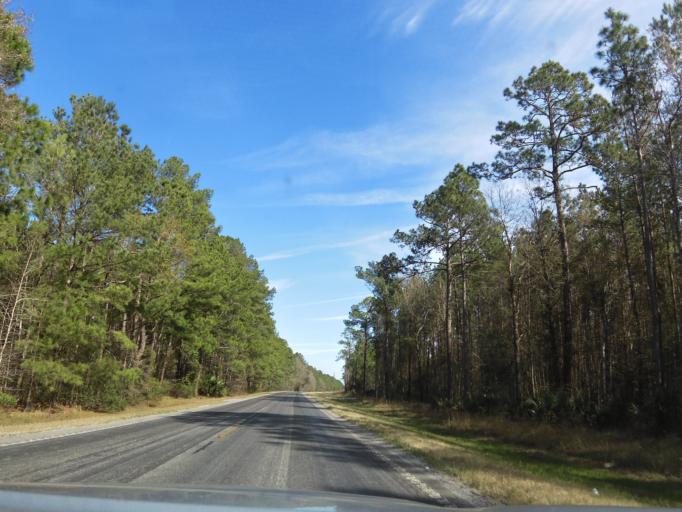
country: US
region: Georgia
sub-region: Glynn County
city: Dock Junction
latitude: 31.2075
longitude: -81.6898
